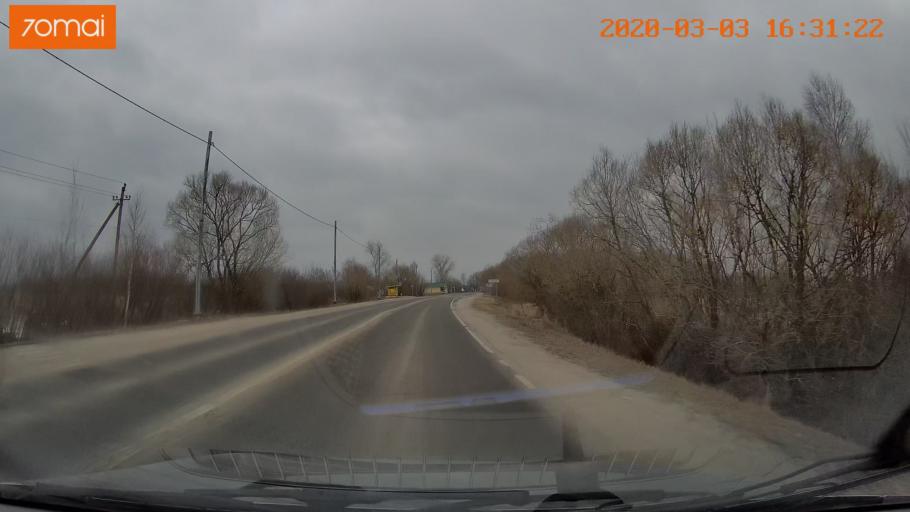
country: RU
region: Moskovskaya
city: Konobeyevo
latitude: 55.4257
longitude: 38.7242
